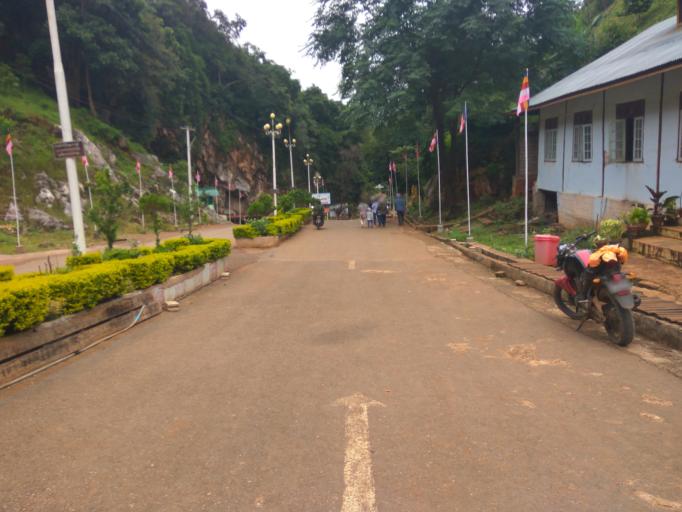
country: MM
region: Shan
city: Taunggyi
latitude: 20.8182
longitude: 97.3354
